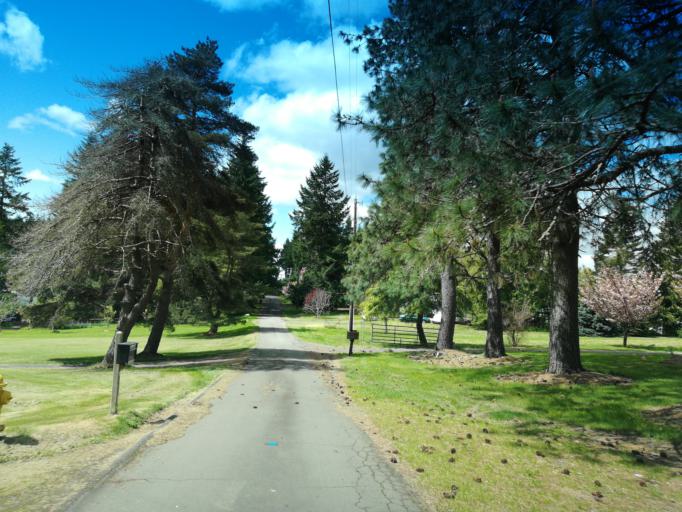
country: US
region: Oregon
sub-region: Clackamas County
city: Damascus
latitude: 45.4279
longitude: -122.4548
